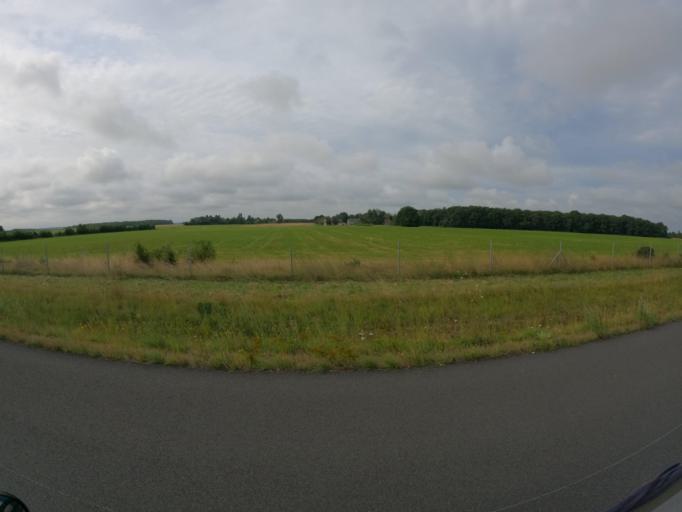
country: FR
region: Centre
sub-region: Departement d'Indre-et-Loire
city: Ballan-Mire
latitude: 47.3078
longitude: 0.6087
